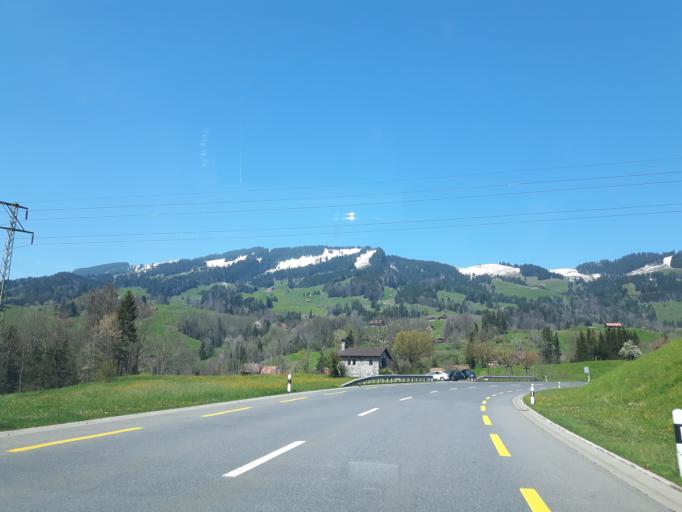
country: CH
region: Schwyz
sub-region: Bezirk Schwyz
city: Sattel
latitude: 47.0688
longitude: 8.6231
